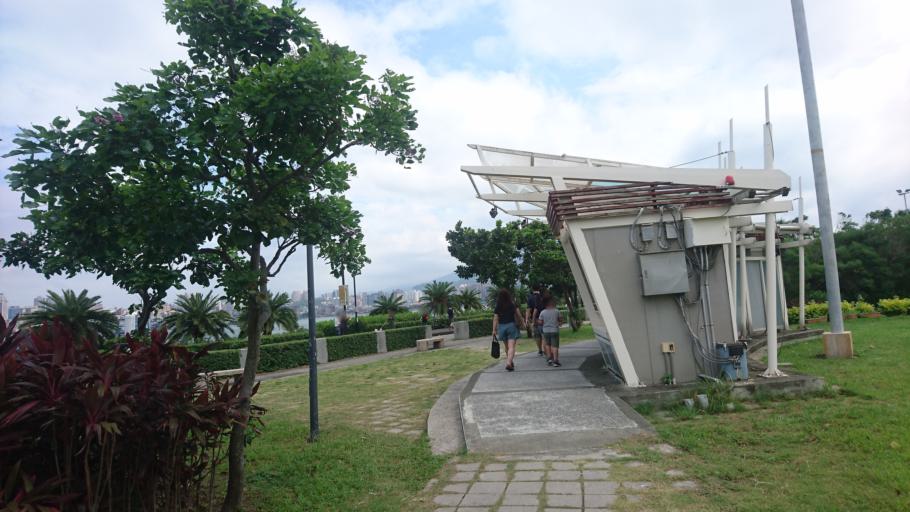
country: TW
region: Taipei
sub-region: Taipei
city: Banqiao
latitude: 25.1607
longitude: 121.4316
